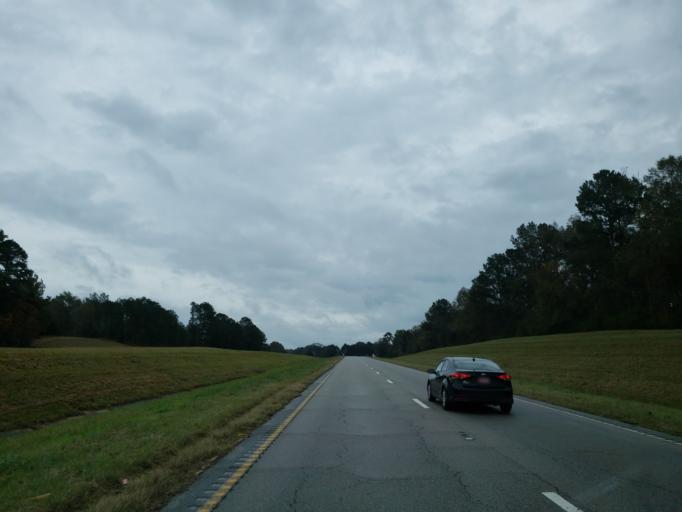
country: US
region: Mississippi
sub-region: Jones County
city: Sharon
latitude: 31.6988
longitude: -88.8986
